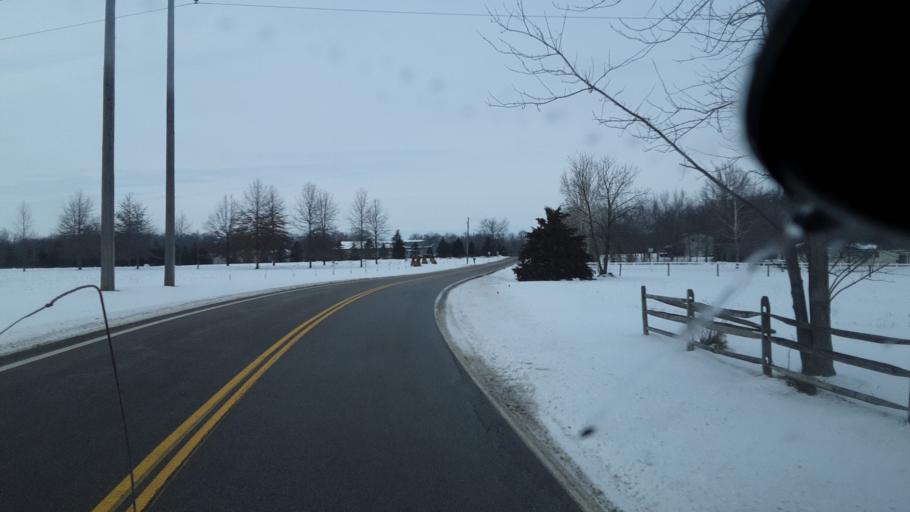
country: US
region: Ohio
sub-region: Madison County
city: Plain City
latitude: 40.1462
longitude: -83.3419
